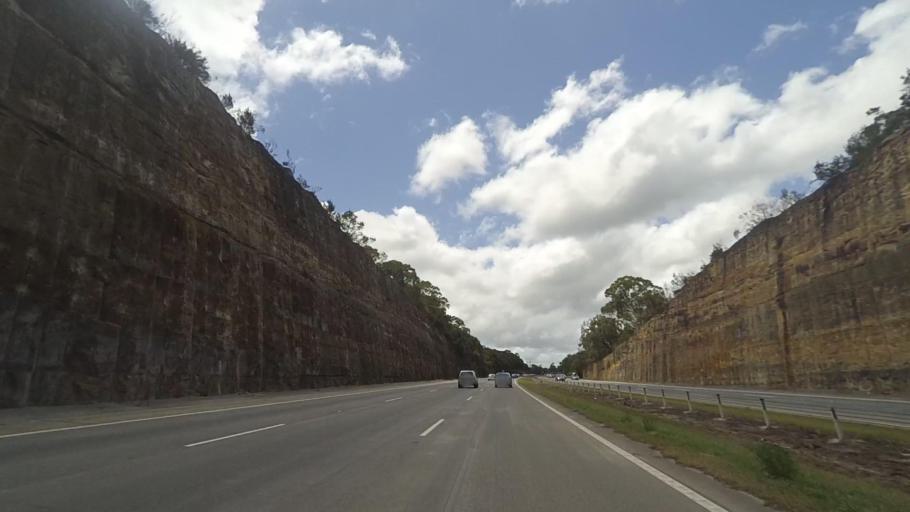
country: AU
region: New South Wales
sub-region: Hornsby Shire
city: Mount Colah
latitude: -33.6659
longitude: 151.1231
